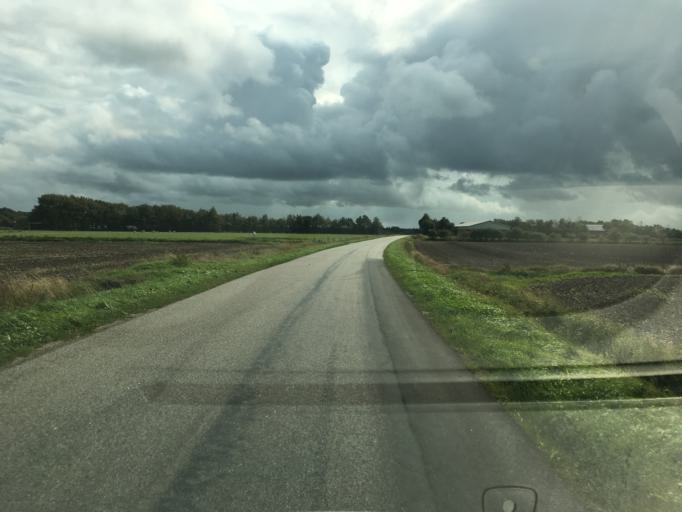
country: DK
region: South Denmark
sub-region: Tonder Kommune
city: Tonder
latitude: 54.9717
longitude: 8.8161
